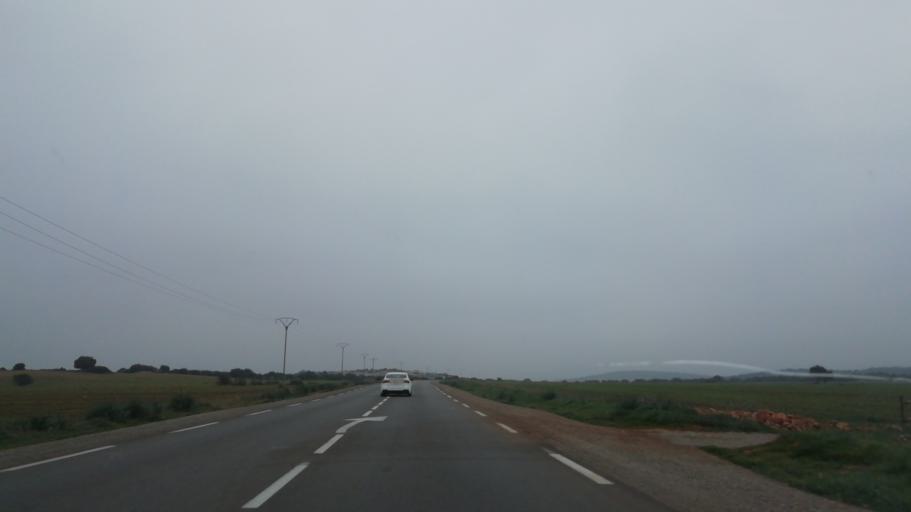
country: DZ
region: Mascara
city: Oued el Abtal
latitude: 35.3028
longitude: 0.4382
